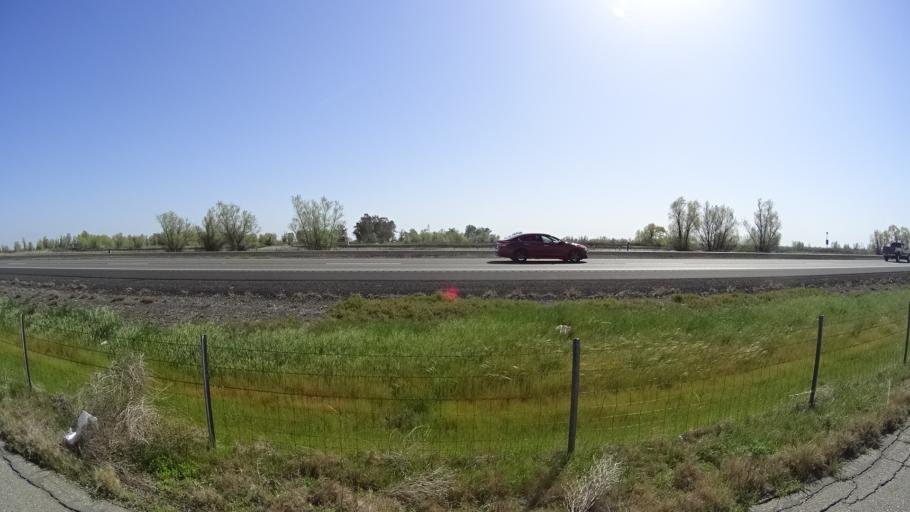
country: US
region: California
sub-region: Glenn County
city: Willows
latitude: 39.4296
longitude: -122.1940
